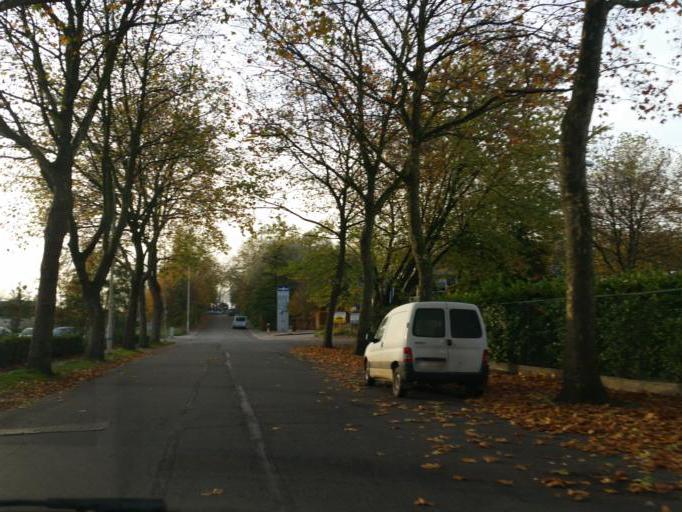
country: BE
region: Flanders
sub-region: Provincie Antwerpen
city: Hoboken
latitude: 51.1794
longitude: 4.3381
